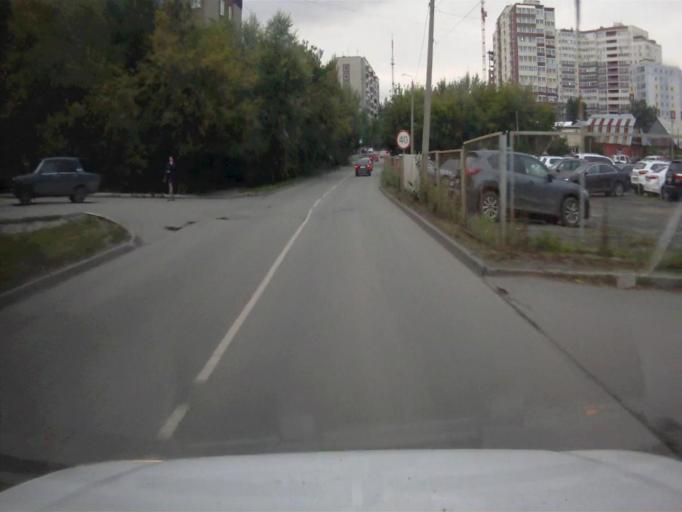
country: RU
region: Chelyabinsk
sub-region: Gorod Chelyabinsk
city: Chelyabinsk
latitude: 55.1431
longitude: 61.3956
